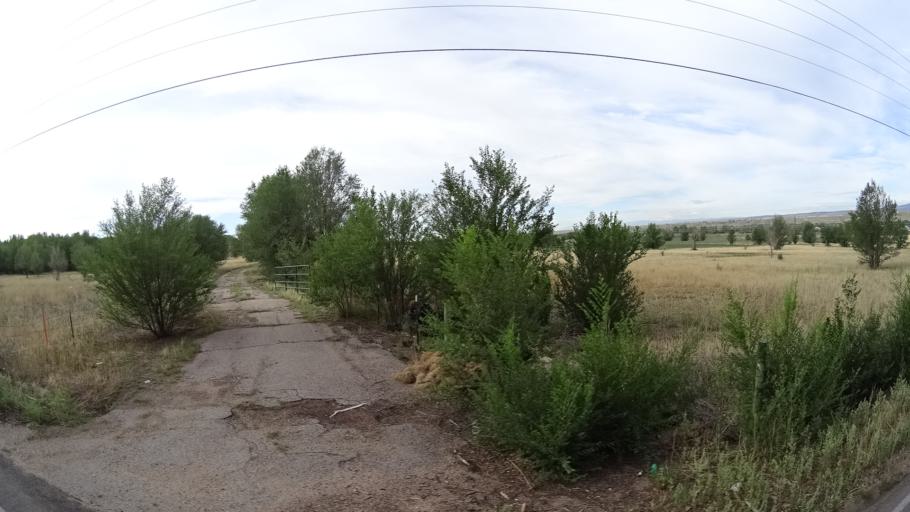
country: US
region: Colorado
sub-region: El Paso County
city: Security-Widefield
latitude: 38.7157
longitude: -104.7081
